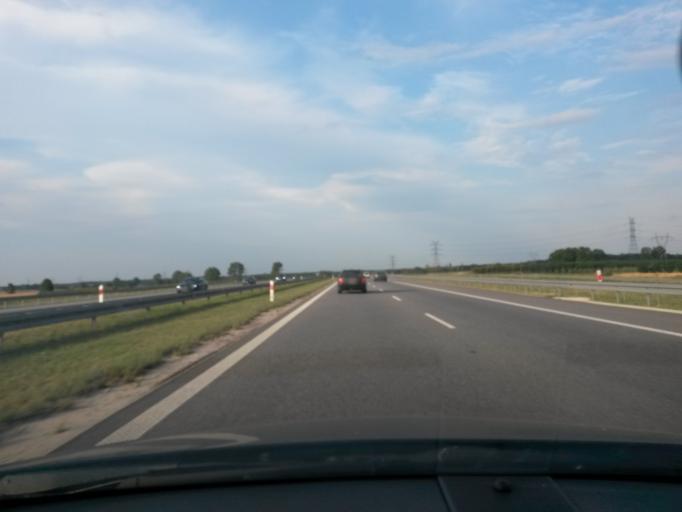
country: PL
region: Lodz Voivodeship
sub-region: Powiat brzezinski
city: Dmosin
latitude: 51.9124
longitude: 19.7489
